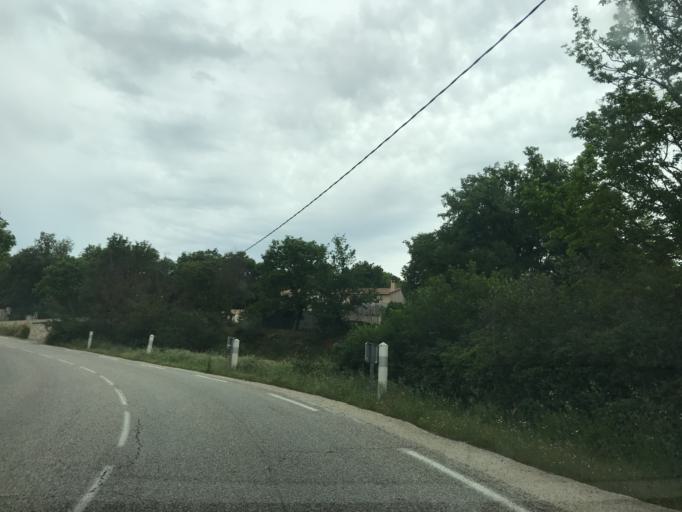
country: FR
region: Provence-Alpes-Cote d'Azur
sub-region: Departement du Var
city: Ginasservis
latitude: 43.6618
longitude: 5.8521
